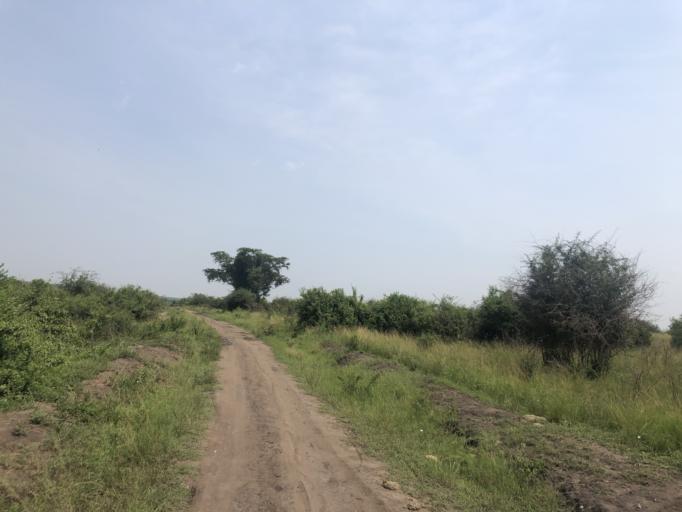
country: UG
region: Western Region
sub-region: Rubirizi District
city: Rubirizi
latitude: -0.2124
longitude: 29.9537
